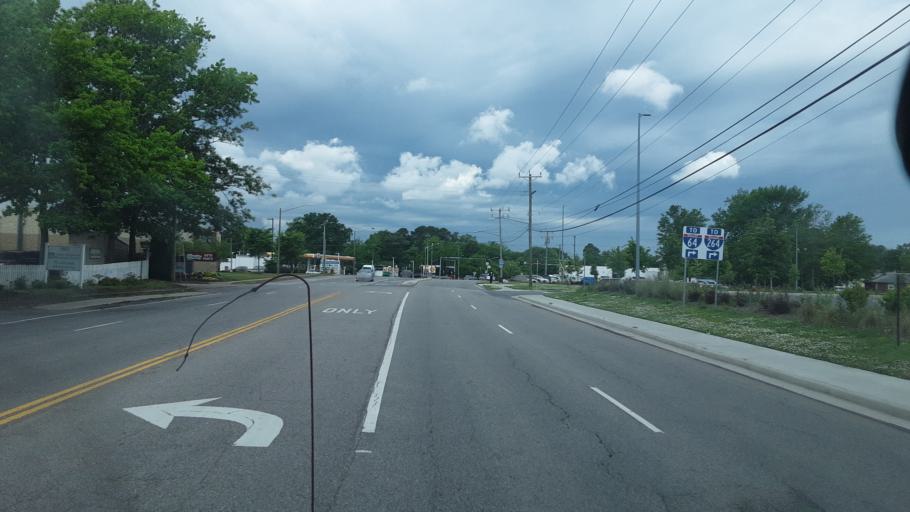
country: US
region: Virginia
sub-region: City of Virginia Beach
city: Virginia Beach
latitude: 36.8420
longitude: -75.9935
